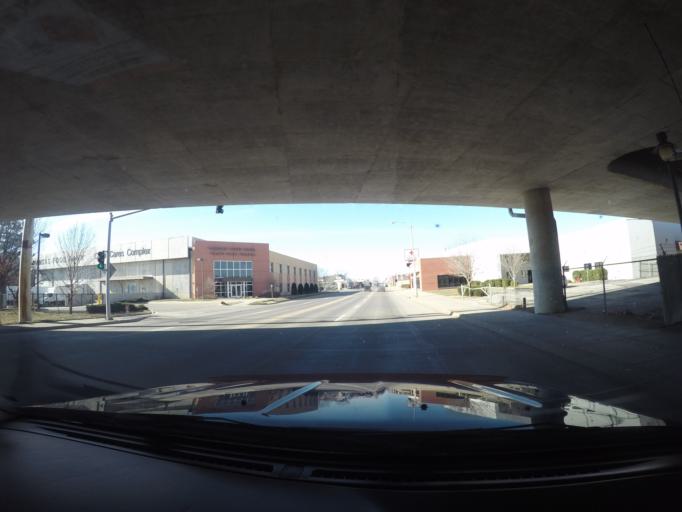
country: US
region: Kansas
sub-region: Sedgwick County
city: Wichita
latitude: 37.6862
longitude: -97.3135
